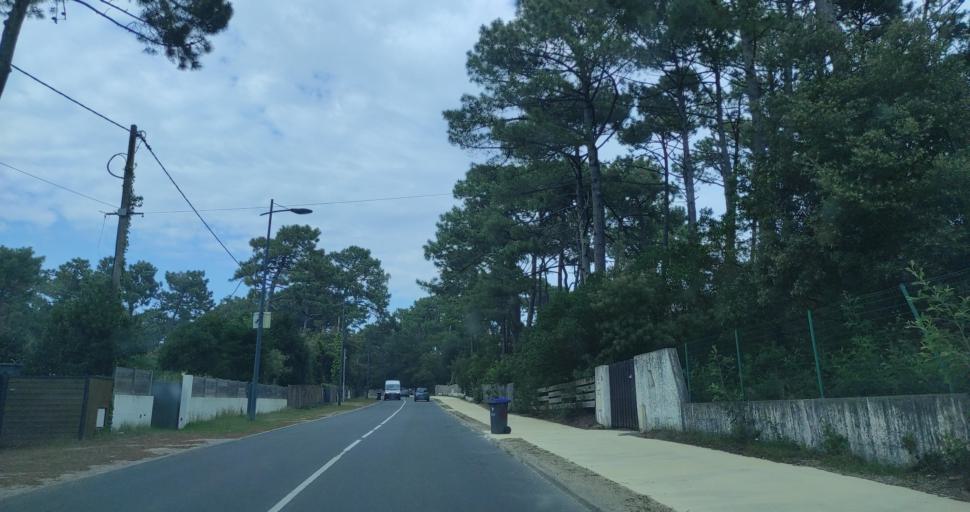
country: FR
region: Aquitaine
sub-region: Departement de la Gironde
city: Arcachon
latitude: 44.6768
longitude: -1.2404
